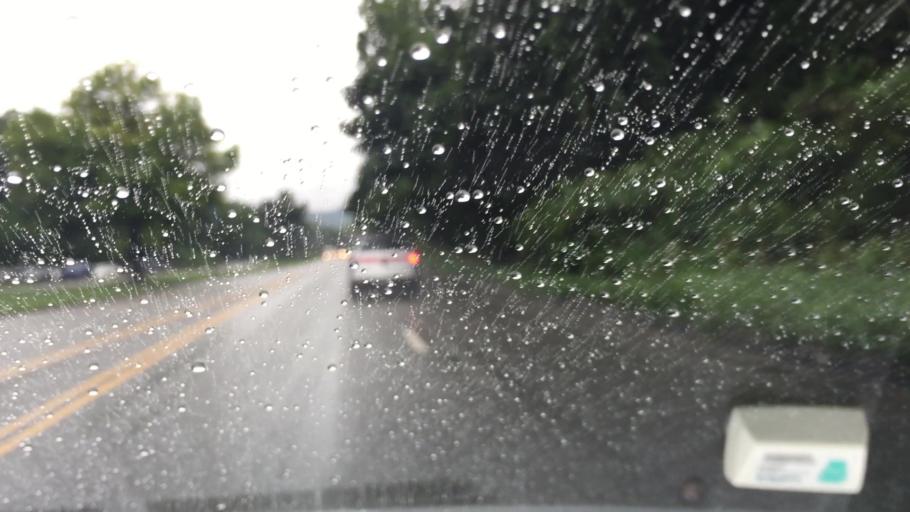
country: US
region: Pennsylvania
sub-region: Allegheny County
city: Aspinwall
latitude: 40.4712
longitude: -79.9085
